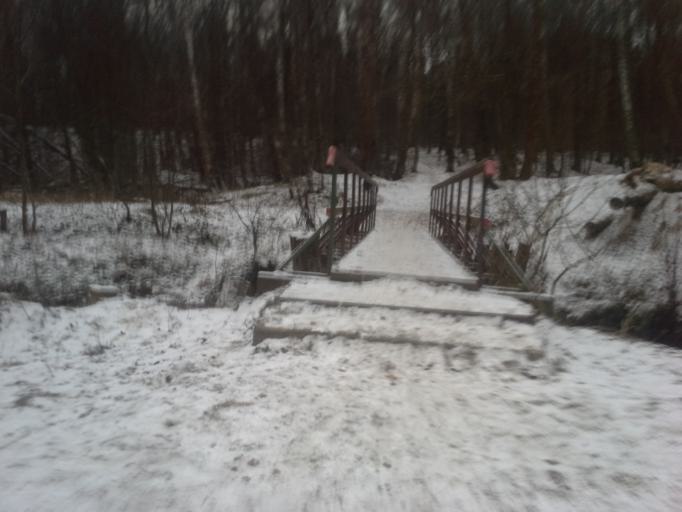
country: RU
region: Moscow
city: Zyuzino
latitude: 55.6307
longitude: 37.5810
